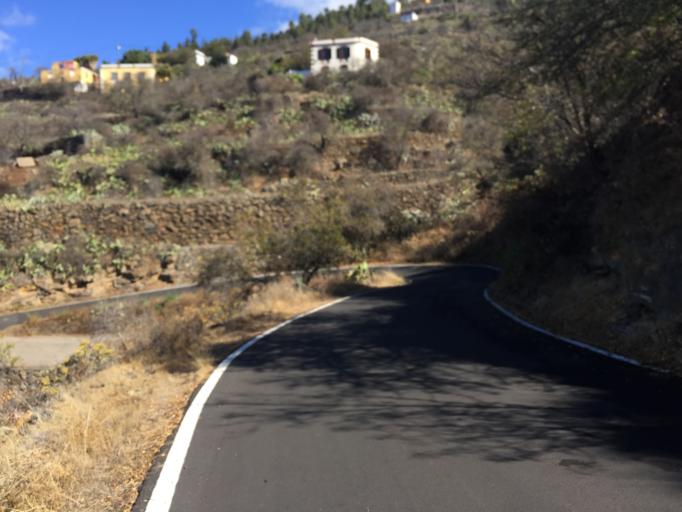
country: ES
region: Canary Islands
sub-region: Provincia de Santa Cruz de Tenerife
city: Tijarafe
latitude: 28.7240
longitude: -17.9639
